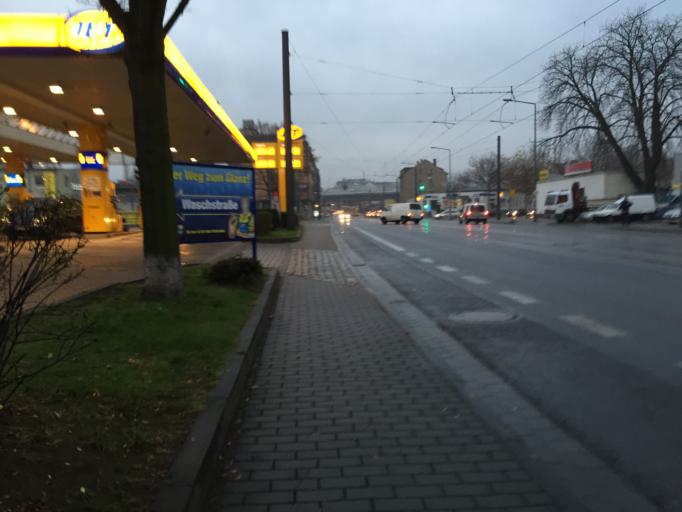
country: DE
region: Saxony
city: Dresden
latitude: 51.0470
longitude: 13.7087
